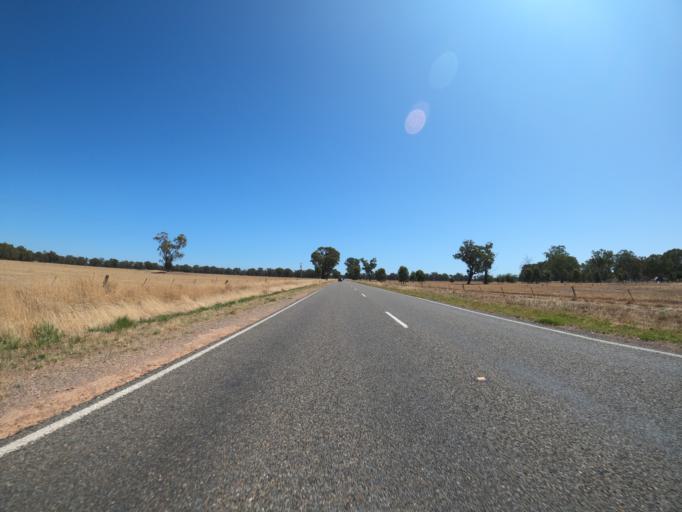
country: AU
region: New South Wales
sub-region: Corowa Shire
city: Corowa
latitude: -36.0771
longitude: 146.3448
